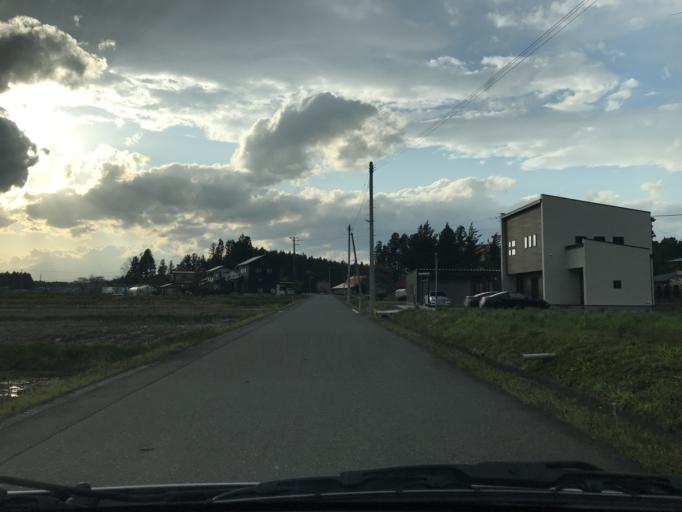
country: JP
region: Iwate
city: Mizusawa
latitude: 39.1025
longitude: 141.1100
